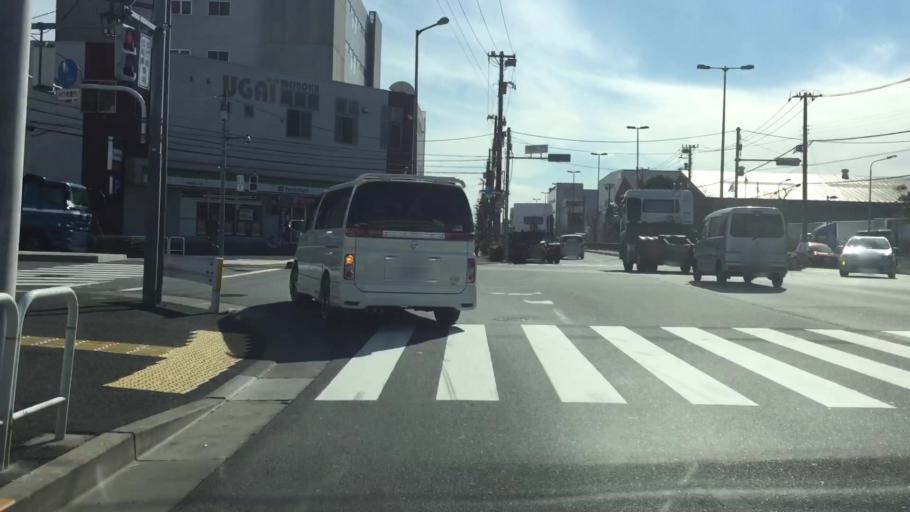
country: JP
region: Tokyo
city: Urayasu
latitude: 35.6386
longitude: 139.8232
